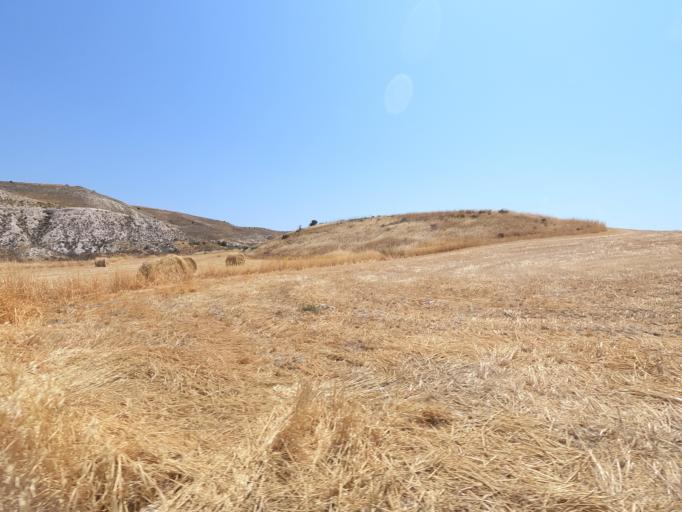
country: CY
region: Larnaka
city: Troulloi
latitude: 35.0371
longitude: 33.6297
